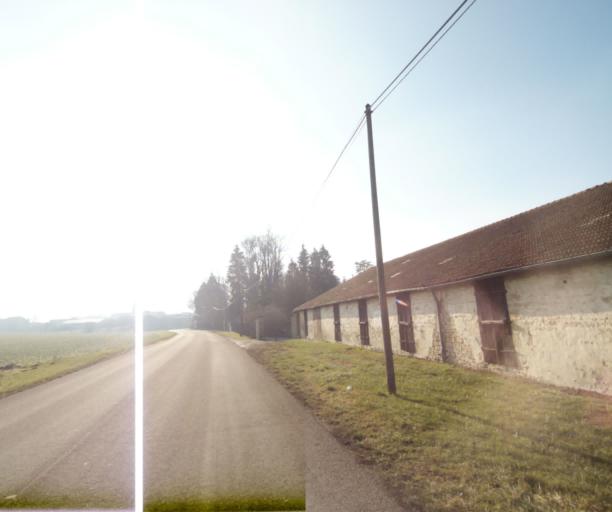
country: FR
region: Champagne-Ardenne
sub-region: Departement de la Haute-Marne
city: Wassy
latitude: 48.4602
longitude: 4.9651
